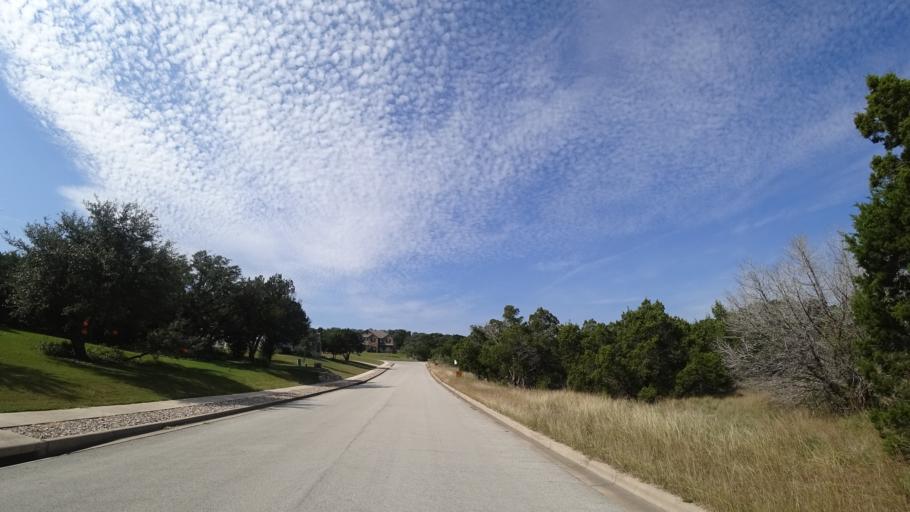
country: US
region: Texas
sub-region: Travis County
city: Bee Cave
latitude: 30.2272
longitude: -97.9314
